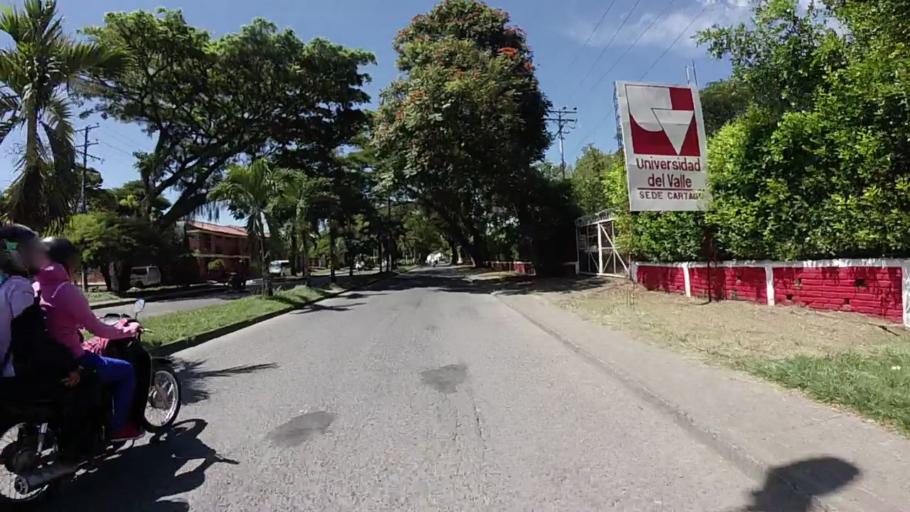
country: CO
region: Valle del Cauca
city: Cartago
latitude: 4.7347
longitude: -75.9104
